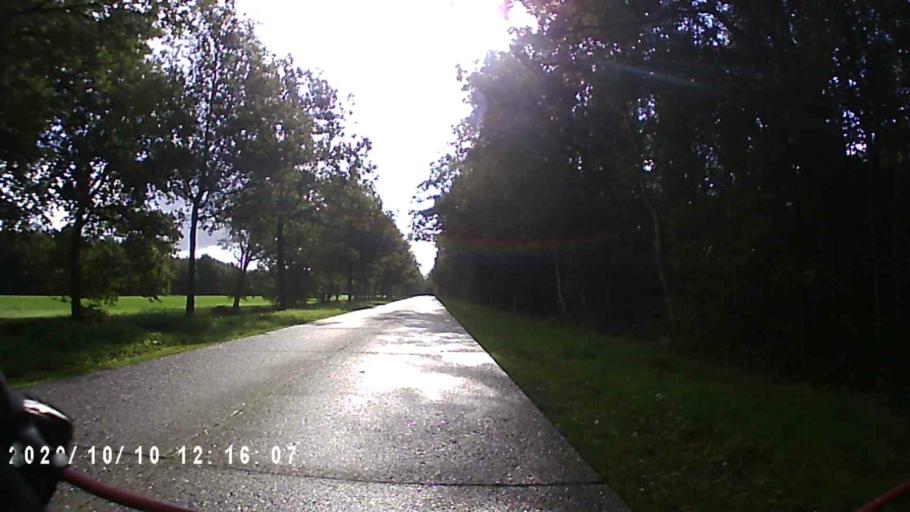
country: NL
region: Friesland
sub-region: Gemeente Heerenveen
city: Jubbega
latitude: 53.0241
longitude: 6.1657
